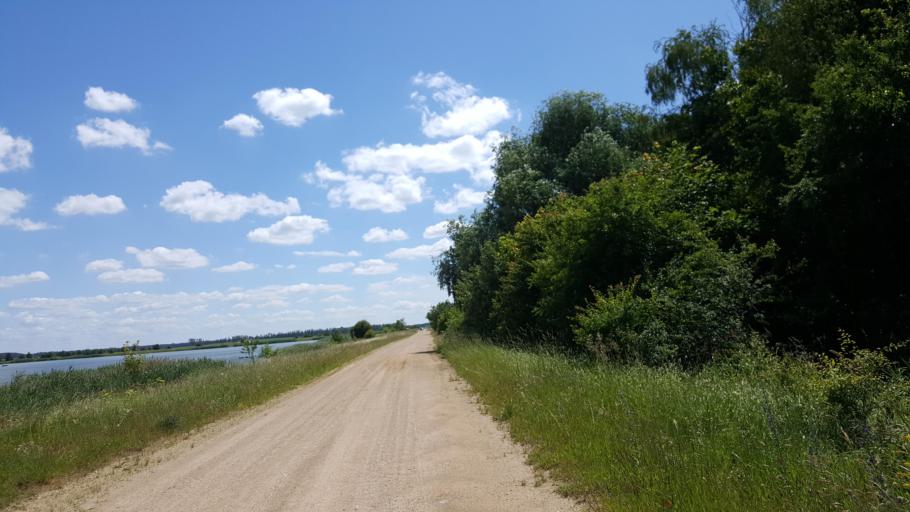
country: BY
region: Brest
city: Vysokaye
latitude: 52.3783
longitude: 23.5476
